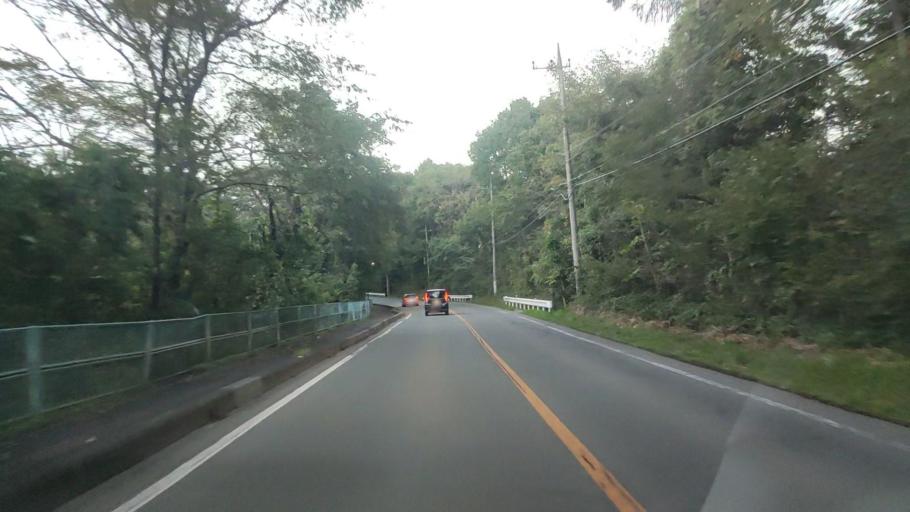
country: JP
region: Nagano
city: Komoro
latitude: 36.4913
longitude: 138.5837
